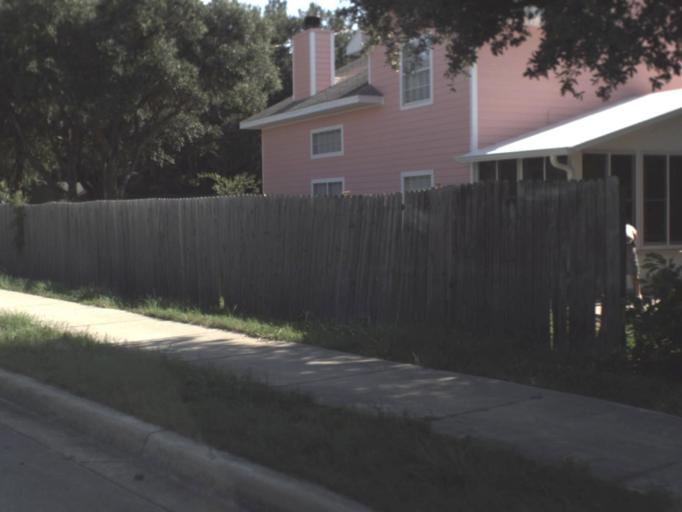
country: US
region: Florida
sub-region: Saint Johns County
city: Saint Augustine Beach
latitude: 29.8487
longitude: -81.2776
